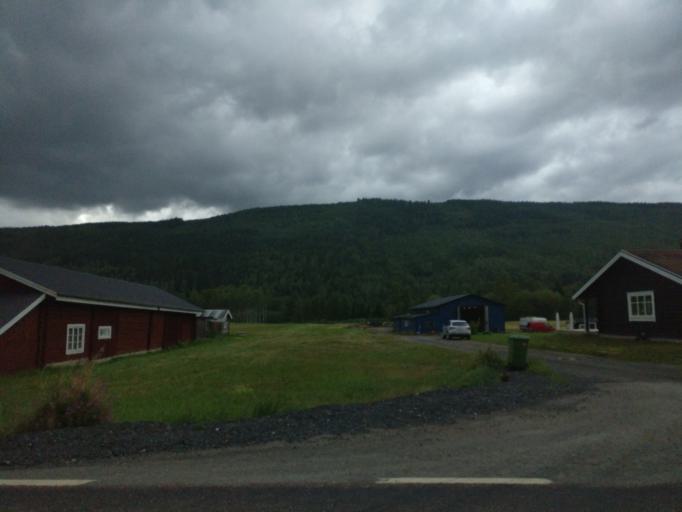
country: SE
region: Vaermland
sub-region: Torsby Kommun
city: Torsby
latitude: 60.7080
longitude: 12.8931
